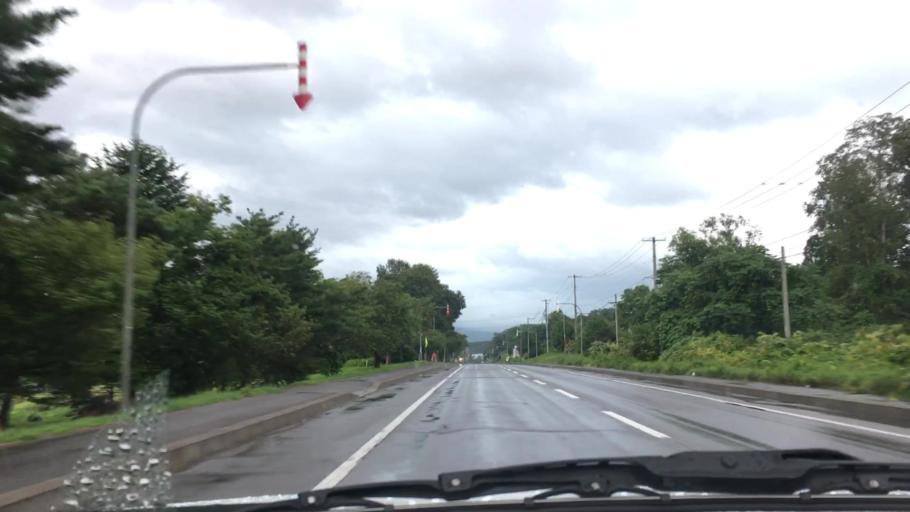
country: JP
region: Hokkaido
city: Nanae
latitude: 42.1106
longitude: 140.5502
